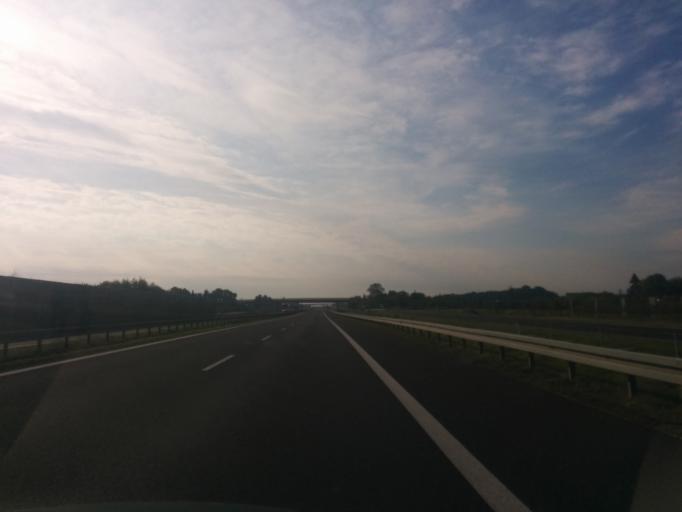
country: PL
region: Masovian Voivodeship
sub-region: Powiat grojecki
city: Jasieniec
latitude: 51.8013
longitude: 20.8887
